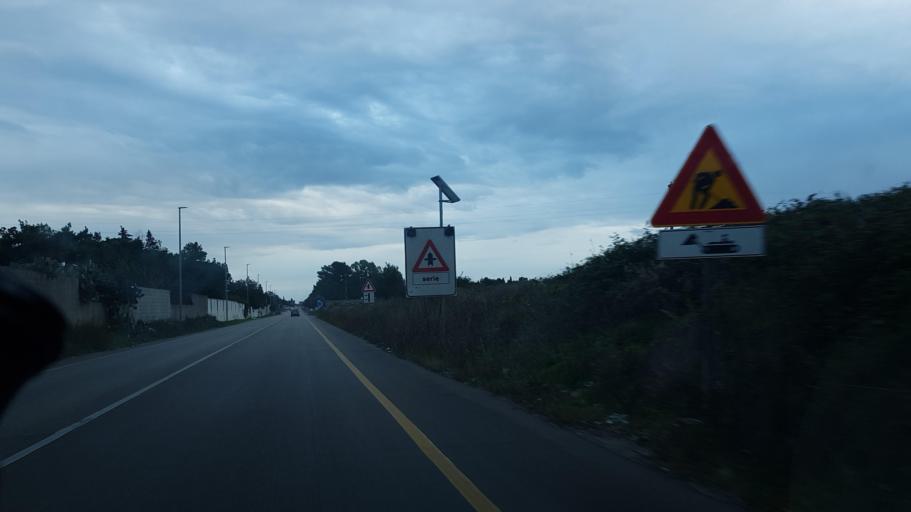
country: IT
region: Apulia
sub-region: Provincia di Lecce
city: Merine
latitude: 40.3424
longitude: 18.2121
